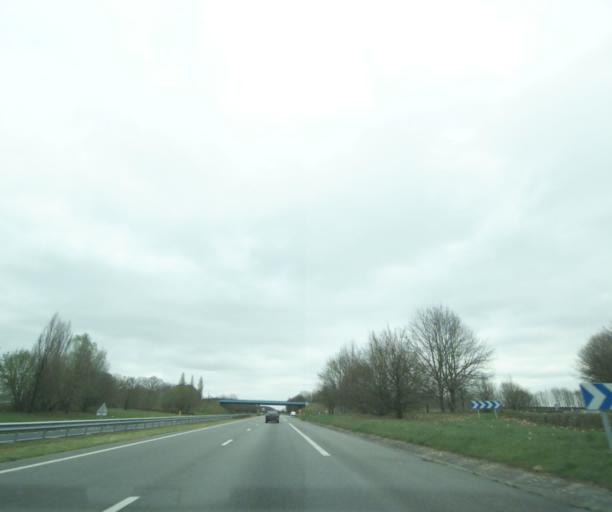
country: FR
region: Limousin
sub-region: Departement de la Correze
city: Uzerche
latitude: 45.3955
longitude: 1.5681
